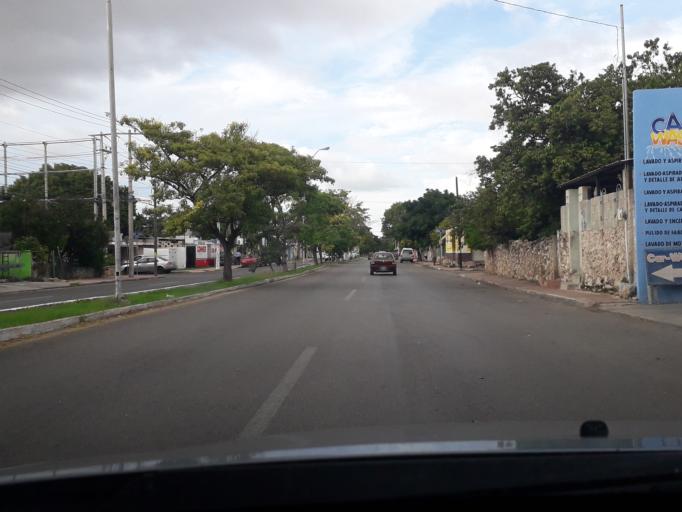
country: MX
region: Yucatan
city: Merida
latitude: 20.9683
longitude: -89.6635
